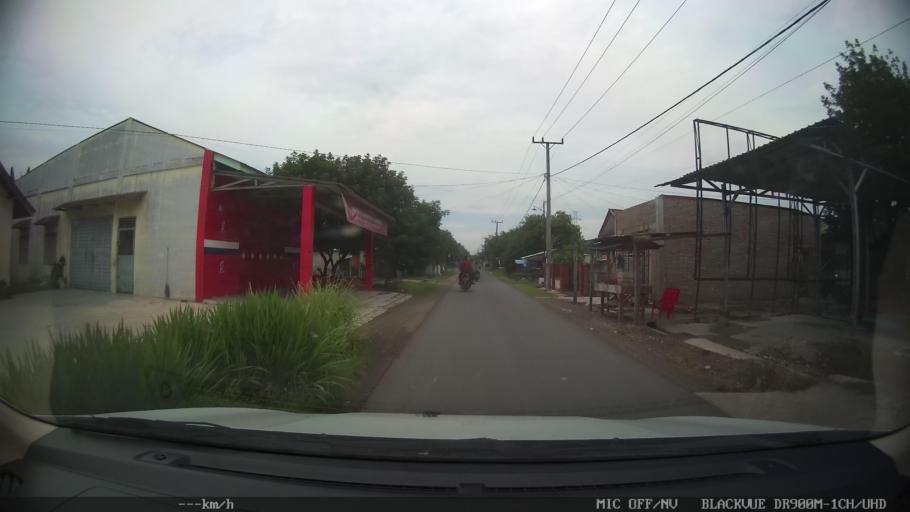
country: ID
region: North Sumatra
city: Sunggal
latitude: 3.6238
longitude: 98.5904
